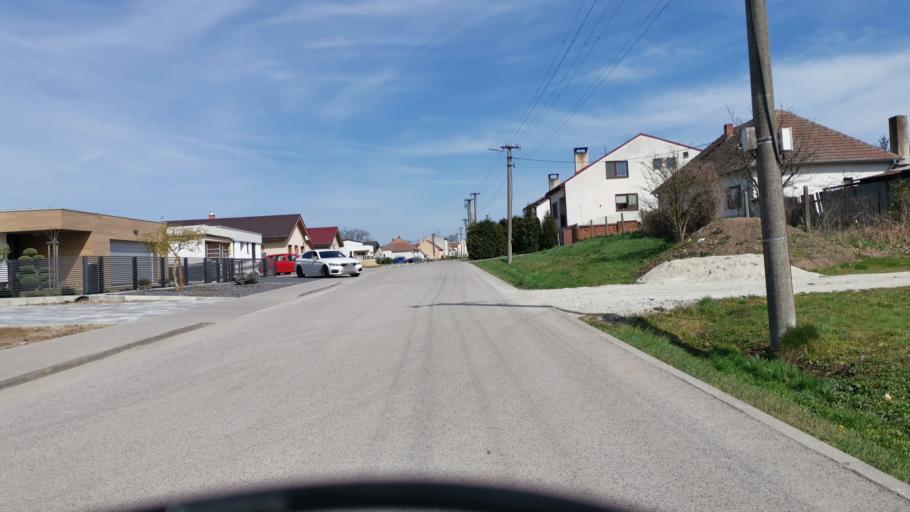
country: SK
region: Trnavsky
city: Gbely
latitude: 48.7162
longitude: 17.1064
